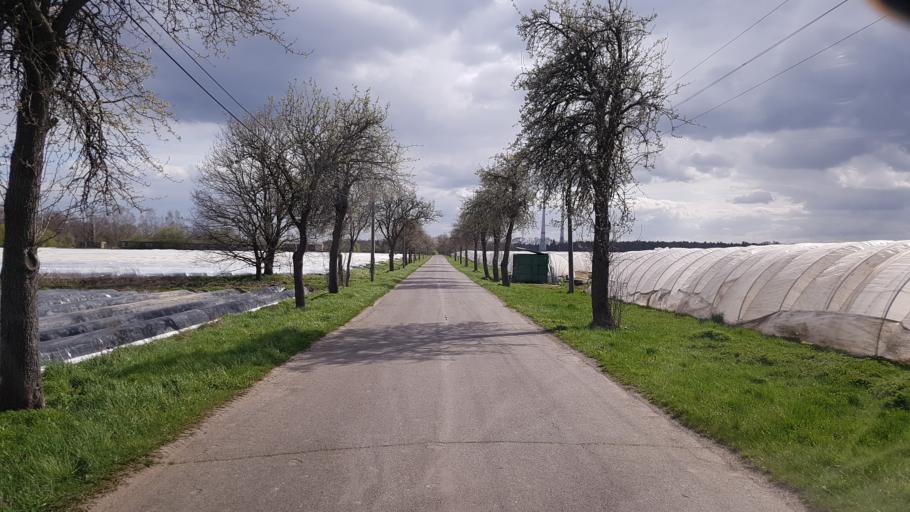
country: DE
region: Brandenburg
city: Calau
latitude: 51.7499
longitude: 14.0031
